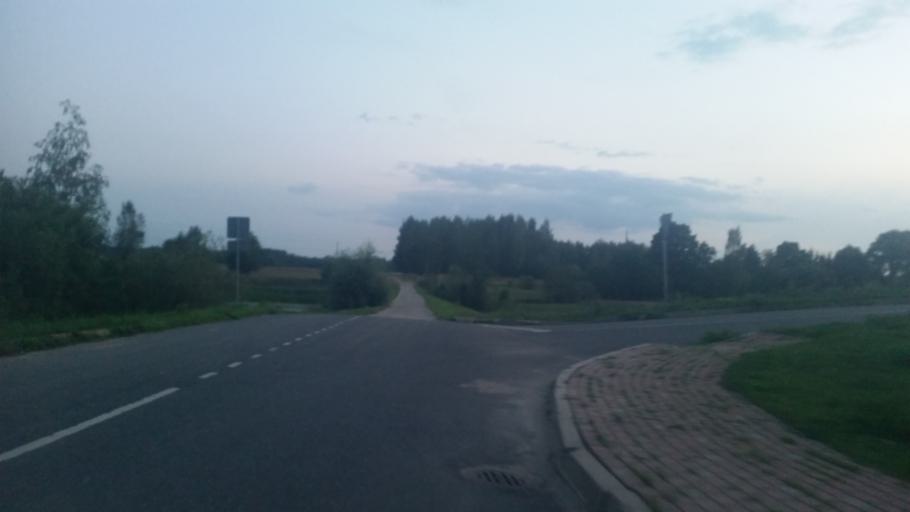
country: LV
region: Ogre
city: Ogre
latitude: 56.8152
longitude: 24.5891
